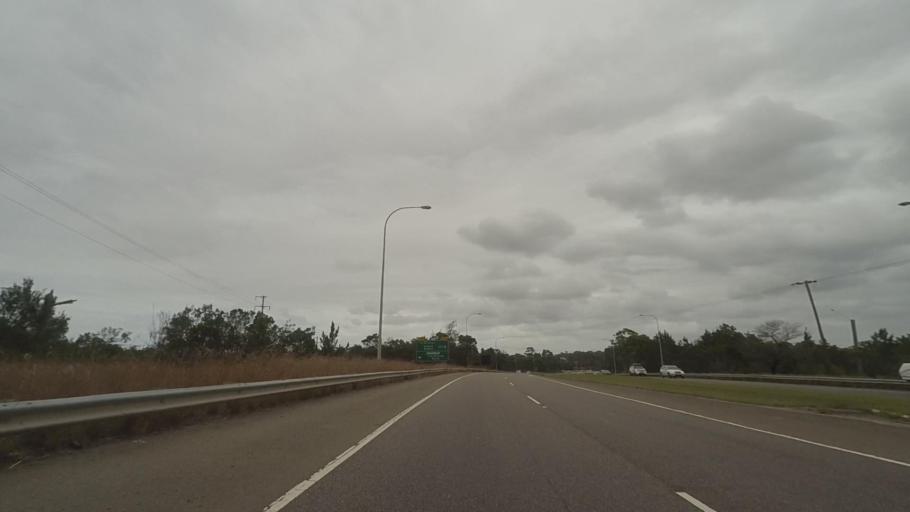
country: AU
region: New South Wales
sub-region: Wyong Shire
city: Buff Point
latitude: -33.2038
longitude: 151.5198
